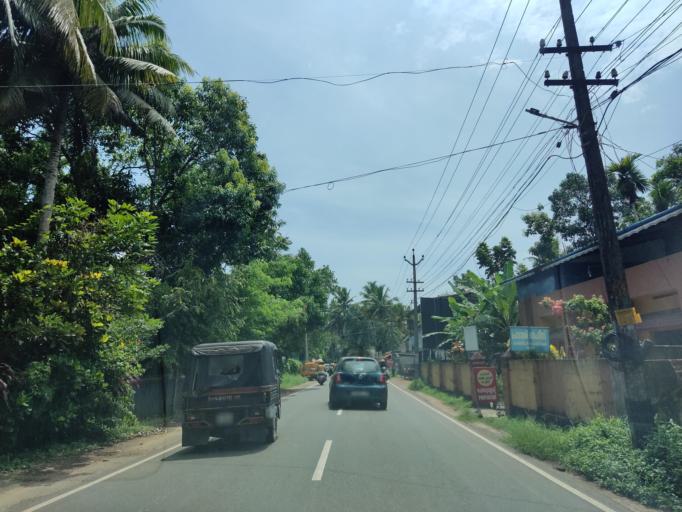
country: IN
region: Kerala
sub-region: Alappuzha
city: Chengannur
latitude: 9.3079
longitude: 76.5932
